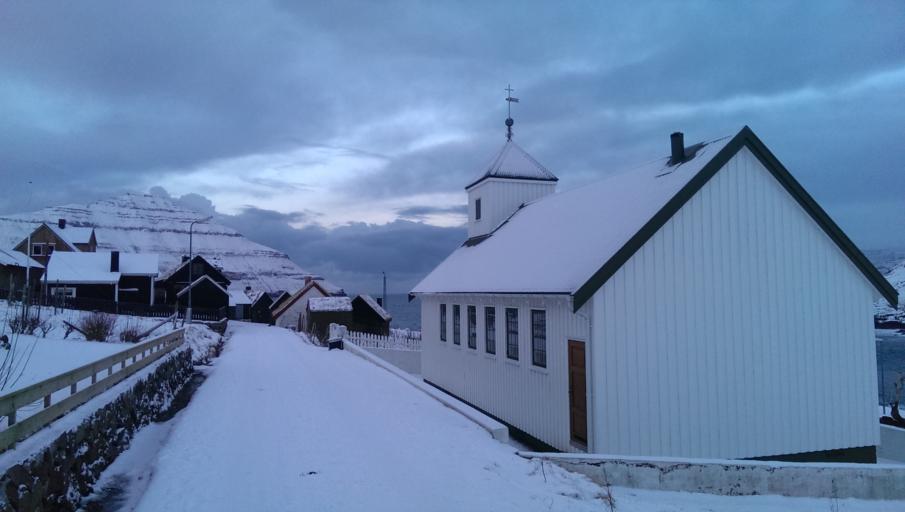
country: FO
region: Eysturoy
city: Fuglafjordur
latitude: 62.2822
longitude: -6.9135
